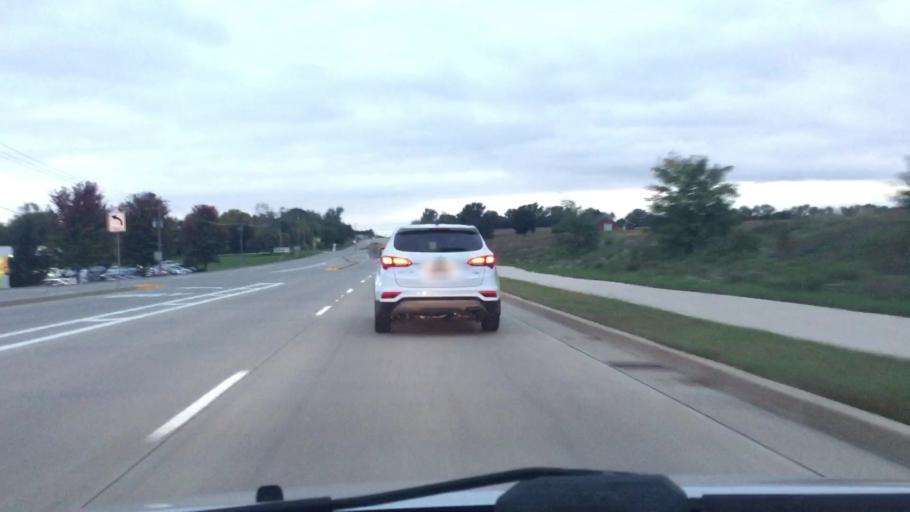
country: US
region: Illinois
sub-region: McHenry County
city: Algonquin
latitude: 42.1949
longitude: -88.2864
